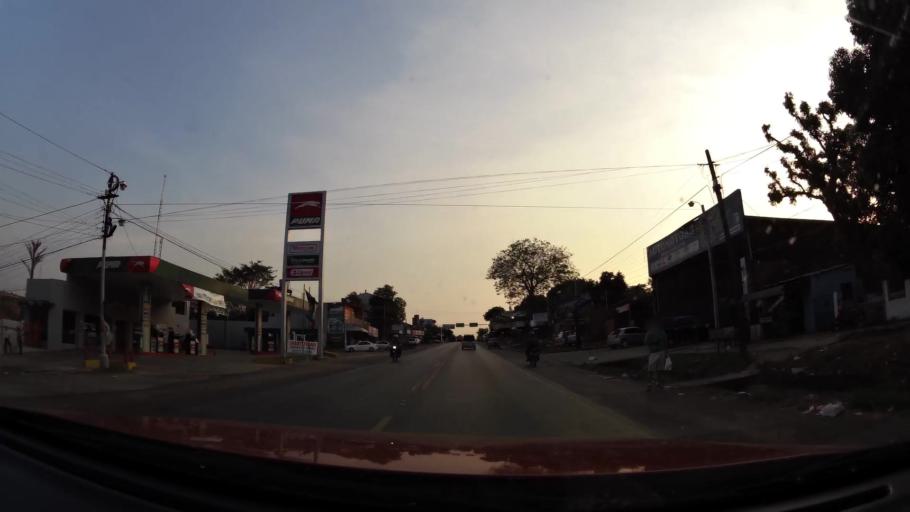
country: PY
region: Central
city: Villa Elisa
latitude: -25.3549
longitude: -57.5940
